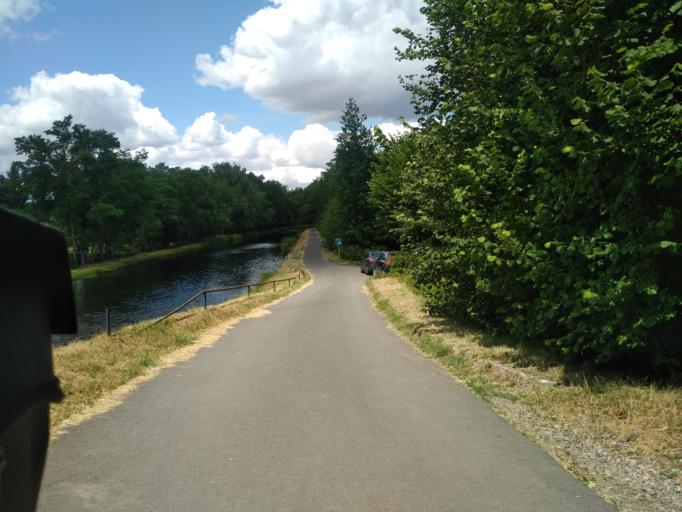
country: FR
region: Rhone-Alpes
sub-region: Departement de la Loire
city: Briennon
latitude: 46.1397
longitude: 4.0808
